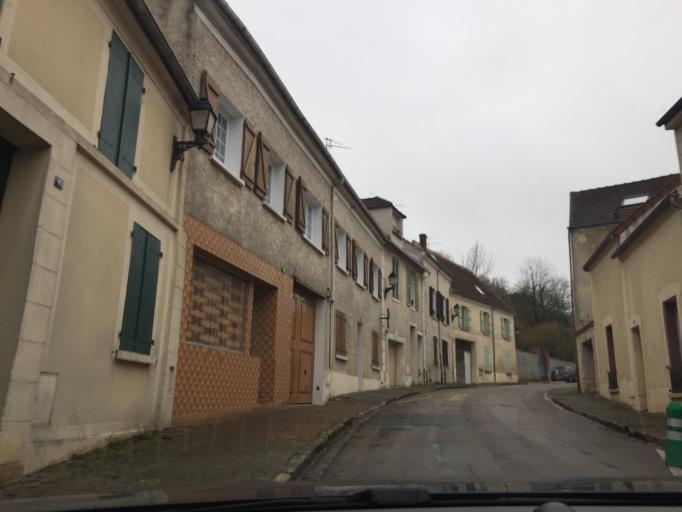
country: FR
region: Ile-de-France
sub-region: Departement de Seine-et-Marne
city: Coupvray
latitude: 48.8924
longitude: 2.7942
